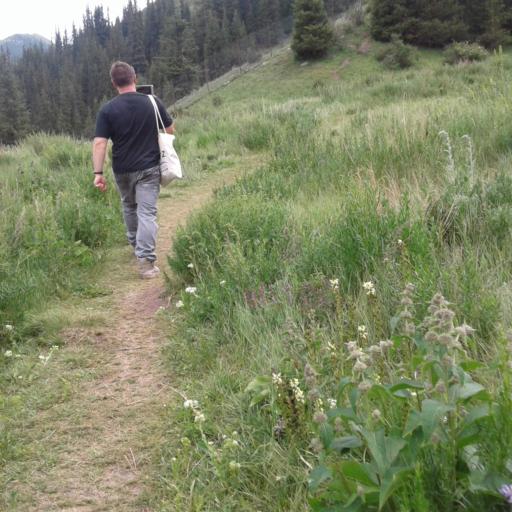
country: KG
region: Naryn
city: Naryn
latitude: 41.4567
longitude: 76.4528
